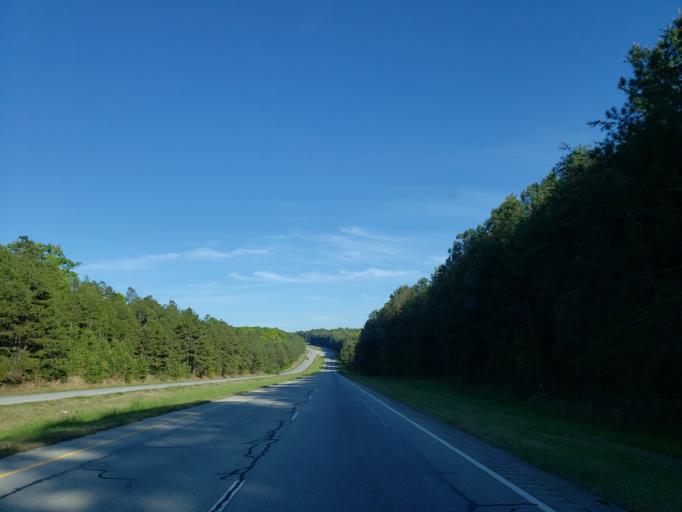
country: US
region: Georgia
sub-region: Polk County
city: Rockmart
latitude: 33.9334
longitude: -84.9646
